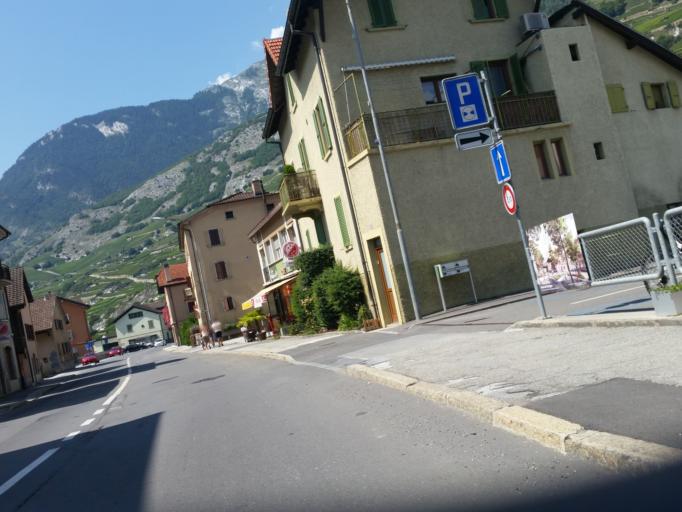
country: CH
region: Valais
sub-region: Conthey District
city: Vetroz
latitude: 46.2258
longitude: 7.2819
